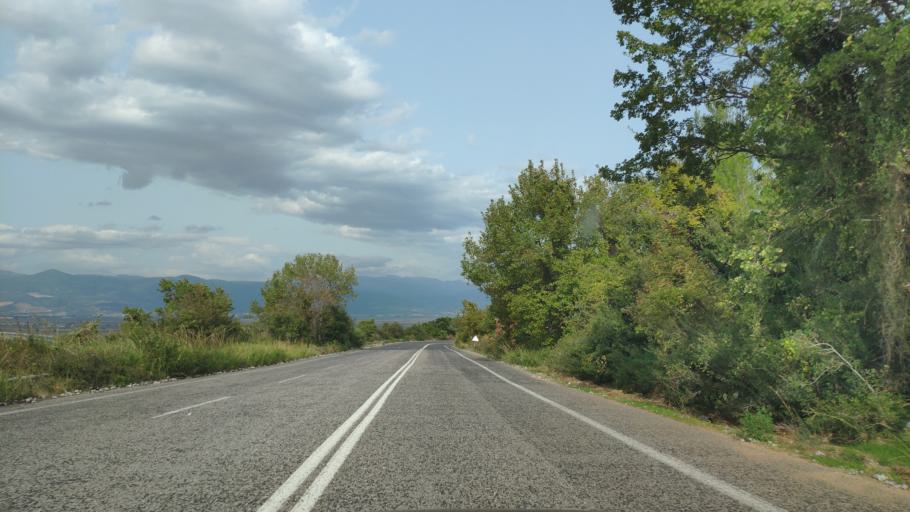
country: GR
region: Central Greece
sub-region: Nomos Fthiotidos
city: Anthili
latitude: 38.7984
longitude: 22.4877
